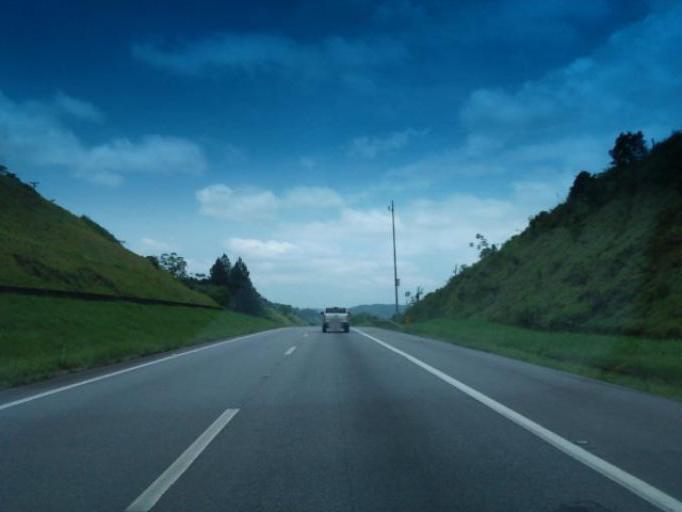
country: BR
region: Sao Paulo
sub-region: Miracatu
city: Miracatu
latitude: -24.1685
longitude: -47.3370
